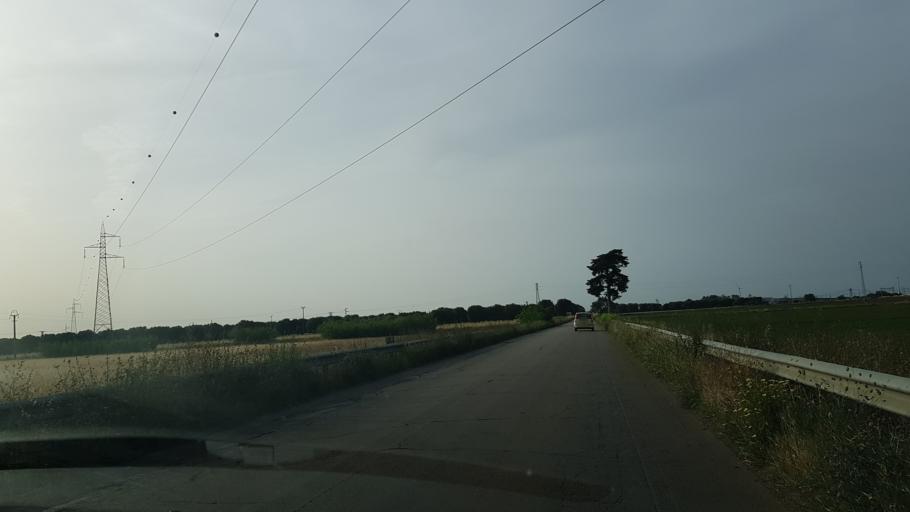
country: IT
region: Apulia
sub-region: Provincia di Brindisi
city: Tuturano
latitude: 40.5376
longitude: 17.9803
